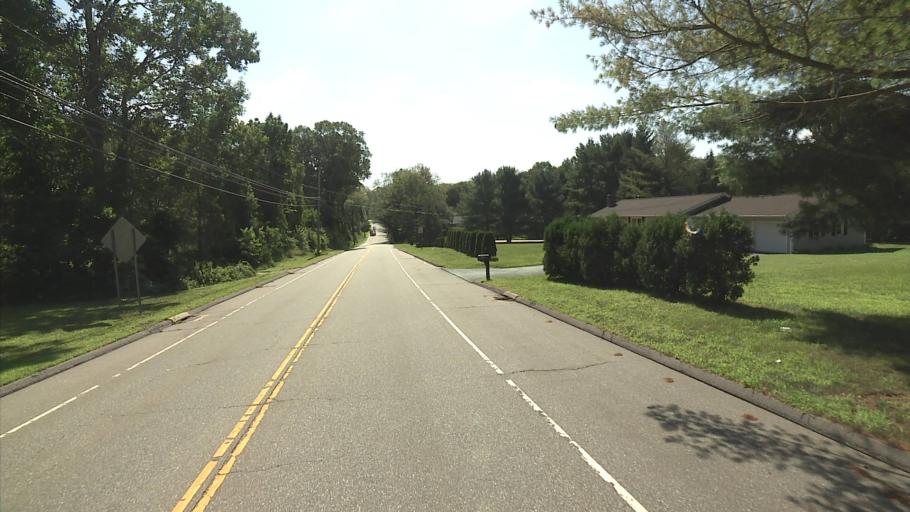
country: US
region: Connecticut
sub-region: Windham County
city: Windham
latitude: 41.7005
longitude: -72.1434
